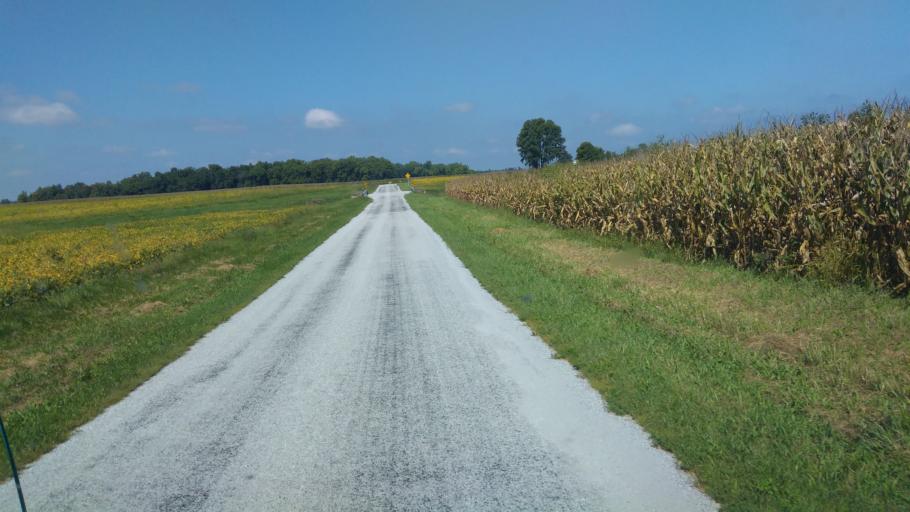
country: US
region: Ohio
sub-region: Hardin County
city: Kenton
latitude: 40.6861
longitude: -83.6093
